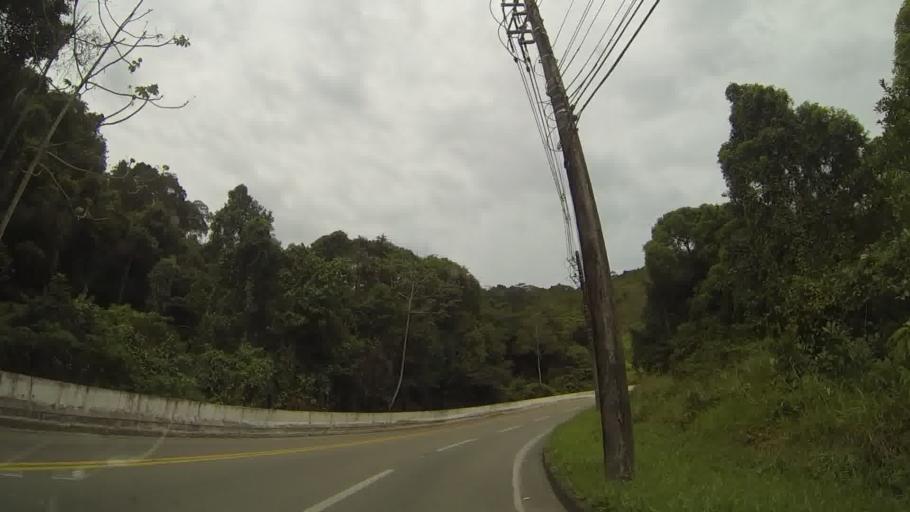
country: BR
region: Sao Paulo
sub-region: Sao Sebastiao
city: Sao Sebastiao
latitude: -23.7939
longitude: -45.5494
